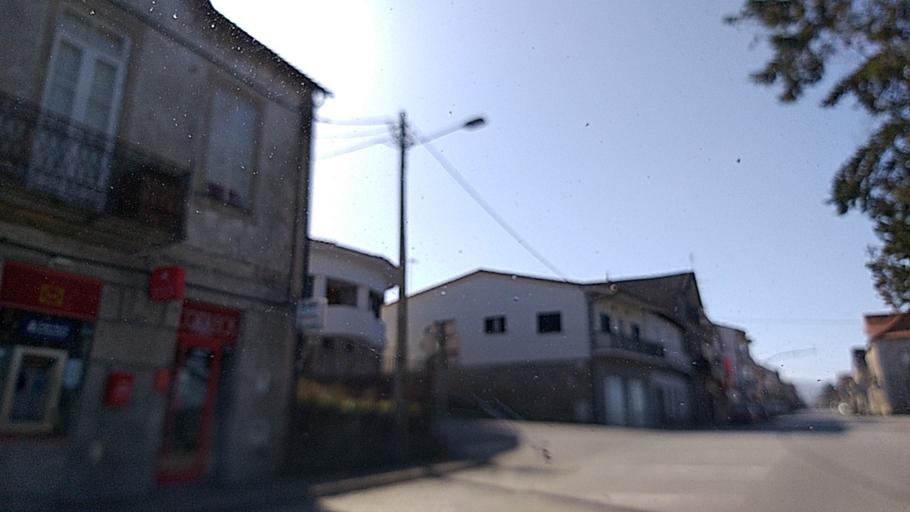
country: PT
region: Guarda
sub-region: Celorico da Beira
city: Celorico da Beira
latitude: 40.6666
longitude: -7.3812
